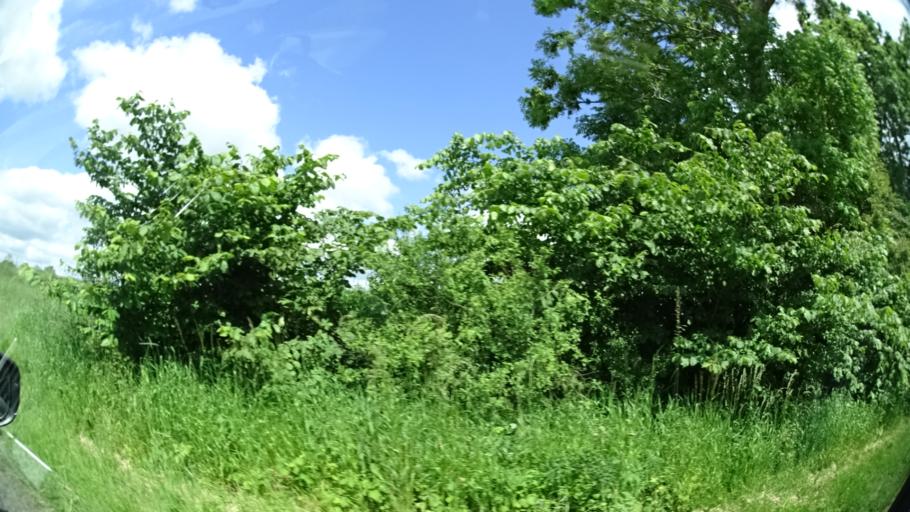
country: DK
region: Central Jutland
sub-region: Syddjurs Kommune
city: Ronde
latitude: 56.2911
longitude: 10.4810
